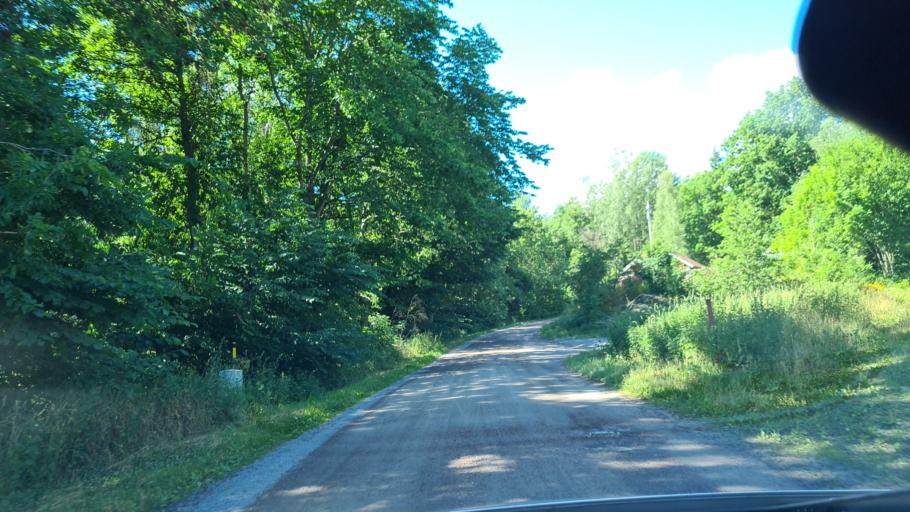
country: SE
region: OEstergoetland
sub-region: Norrkopings Kommun
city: Krokek
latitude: 58.6726
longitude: 16.4233
